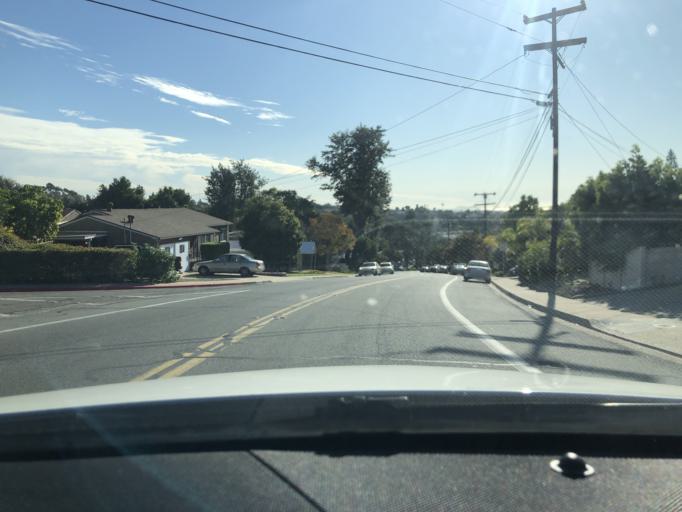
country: US
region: California
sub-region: San Diego County
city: Lemon Grove
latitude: 32.7529
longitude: -117.0719
